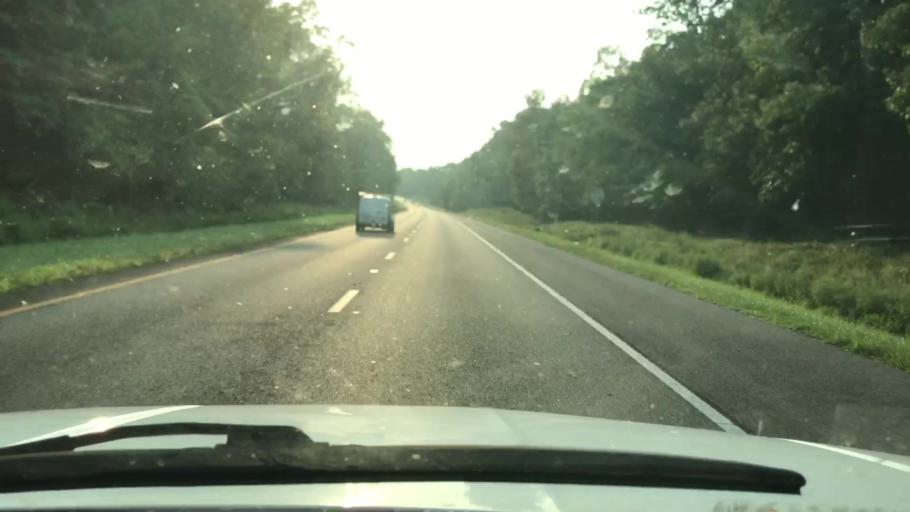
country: US
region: Virginia
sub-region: Chesterfield County
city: Brandermill
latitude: 37.4108
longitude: -77.5773
